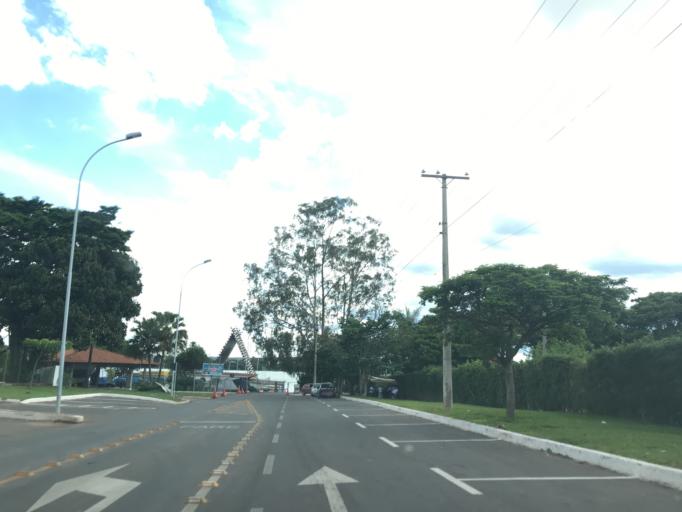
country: BR
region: Federal District
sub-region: Brasilia
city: Brasilia
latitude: -15.8185
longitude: -47.8671
